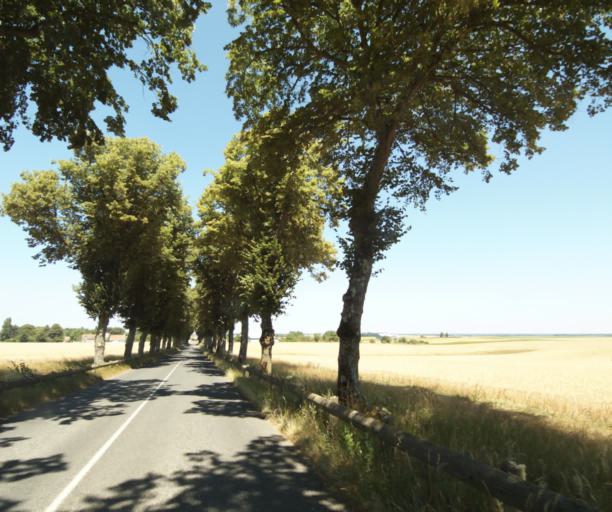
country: FR
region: Ile-de-France
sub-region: Departement de Seine-et-Marne
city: Noisy-sur-Ecole
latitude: 48.3416
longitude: 2.4576
